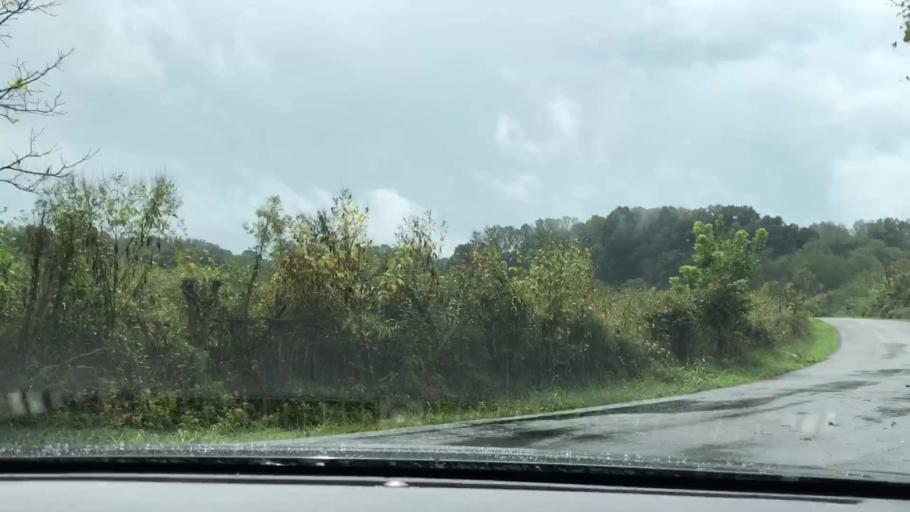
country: US
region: Tennessee
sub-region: Macon County
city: Red Boiling Springs
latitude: 36.6078
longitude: -85.7696
